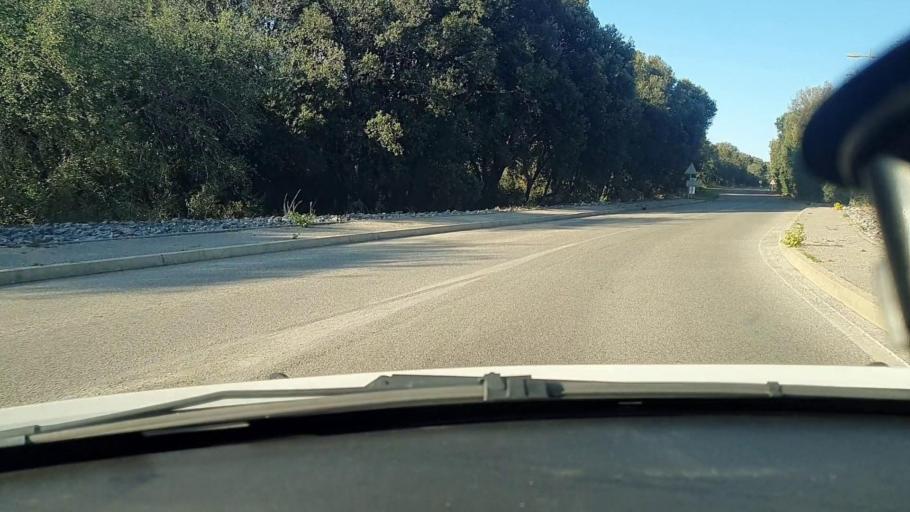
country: FR
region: Languedoc-Roussillon
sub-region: Departement du Gard
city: Barjac
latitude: 44.2251
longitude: 4.3445
